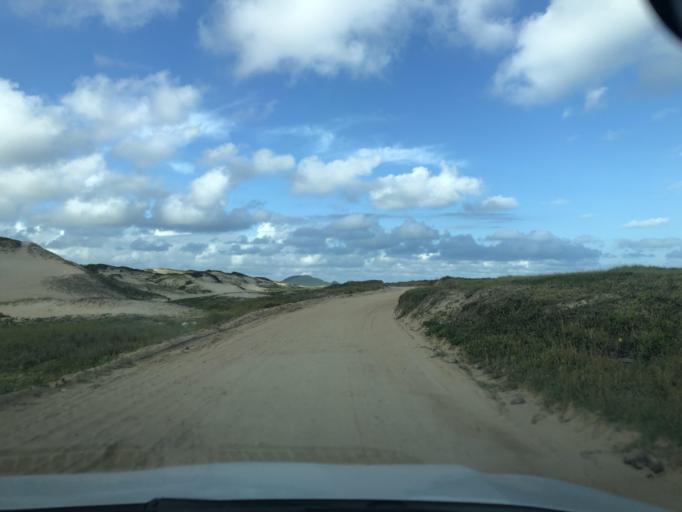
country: BR
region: Santa Catarina
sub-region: Sao Francisco Do Sul
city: Sao Francisco do Sul
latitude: -26.2622
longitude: -48.5202
